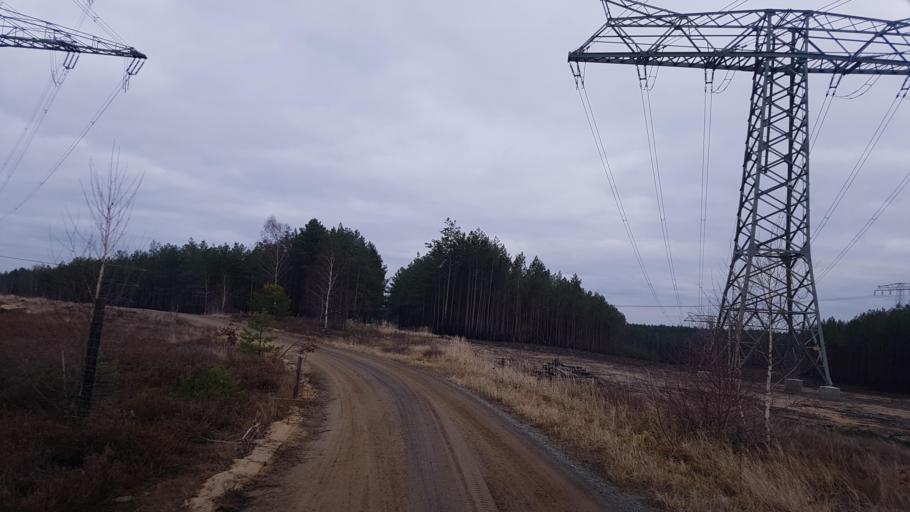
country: DE
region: Brandenburg
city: Altdobern
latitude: 51.6401
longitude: 14.0024
